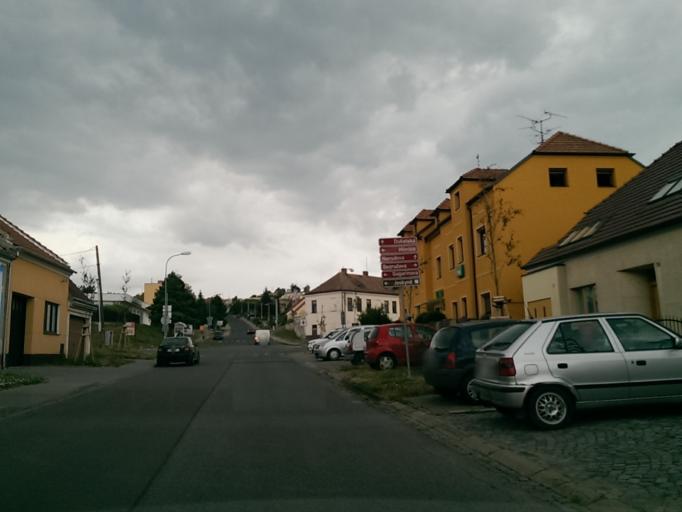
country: CZ
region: South Moravian
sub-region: Okres Breclav
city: Mikulov
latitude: 48.8128
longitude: 16.6456
